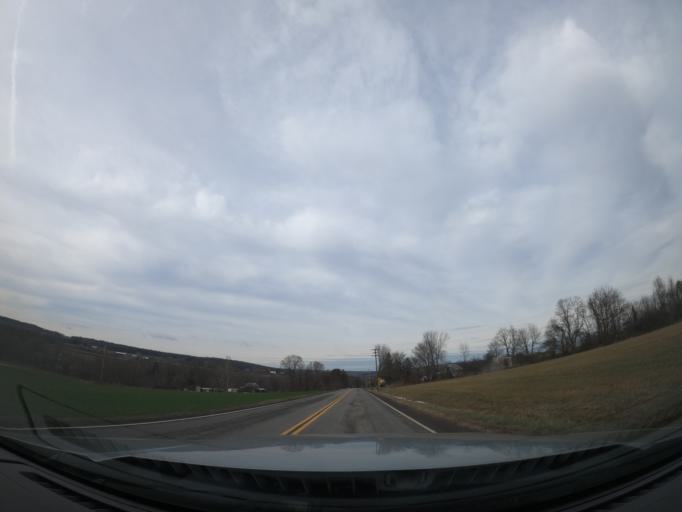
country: US
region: New York
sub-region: Yates County
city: Dundee
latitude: 42.5047
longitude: -76.9587
